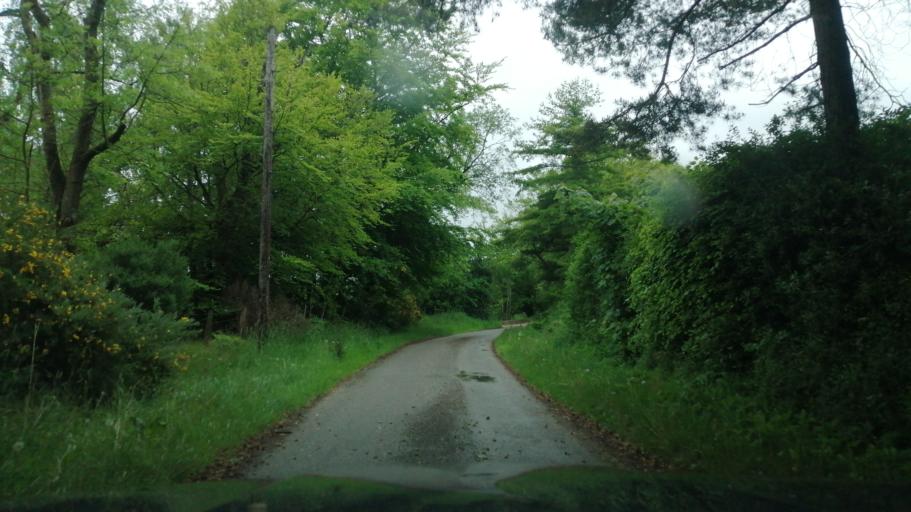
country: GB
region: Scotland
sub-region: Moray
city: Keith
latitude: 57.5582
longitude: -2.8635
